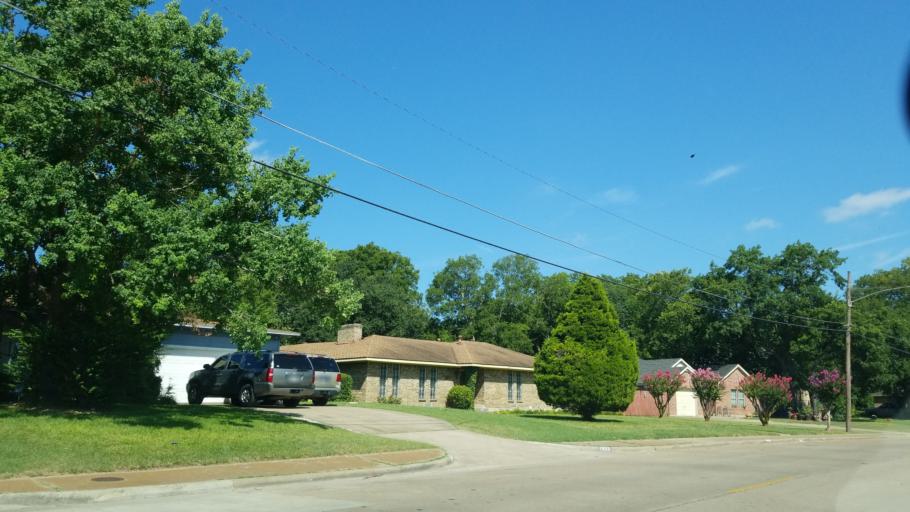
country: US
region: Texas
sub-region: Dallas County
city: Dallas
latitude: 32.7292
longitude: -96.7921
